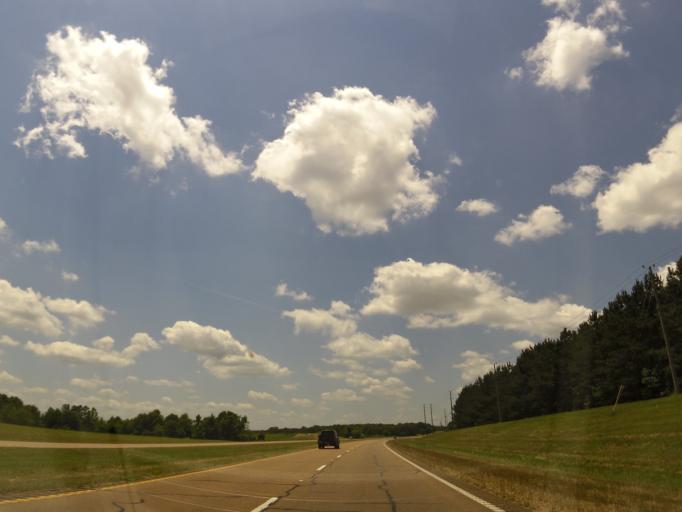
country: US
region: Mississippi
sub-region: Pontotoc County
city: Pontotoc
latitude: 34.2822
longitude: -89.0552
